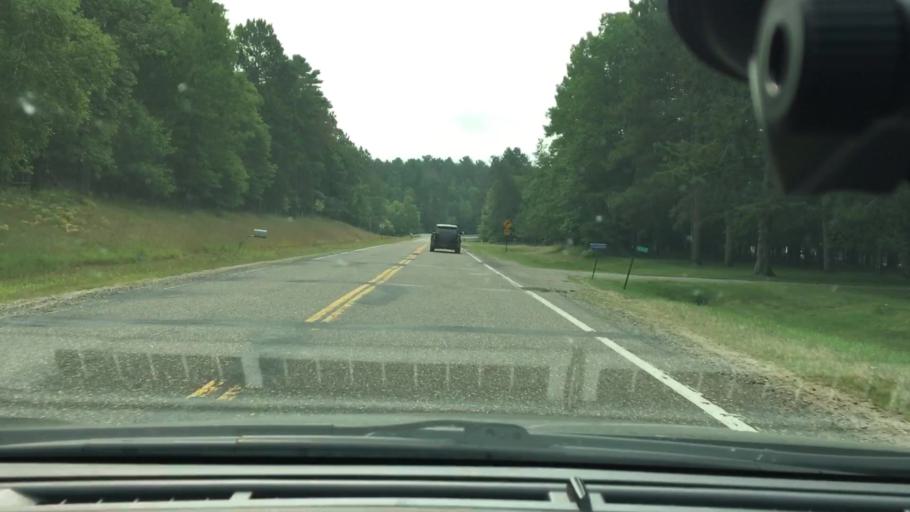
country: US
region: Minnesota
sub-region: Crow Wing County
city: Cross Lake
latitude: 46.6557
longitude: -94.0998
